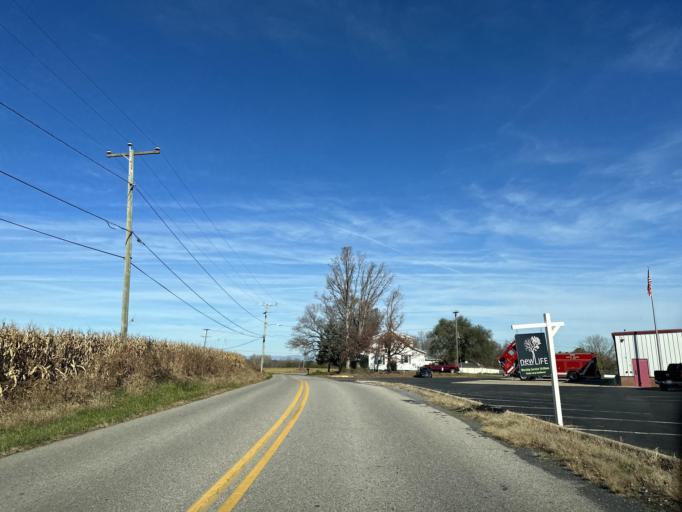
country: US
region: Virginia
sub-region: Augusta County
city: Crimora
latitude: 38.2009
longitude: -78.9043
